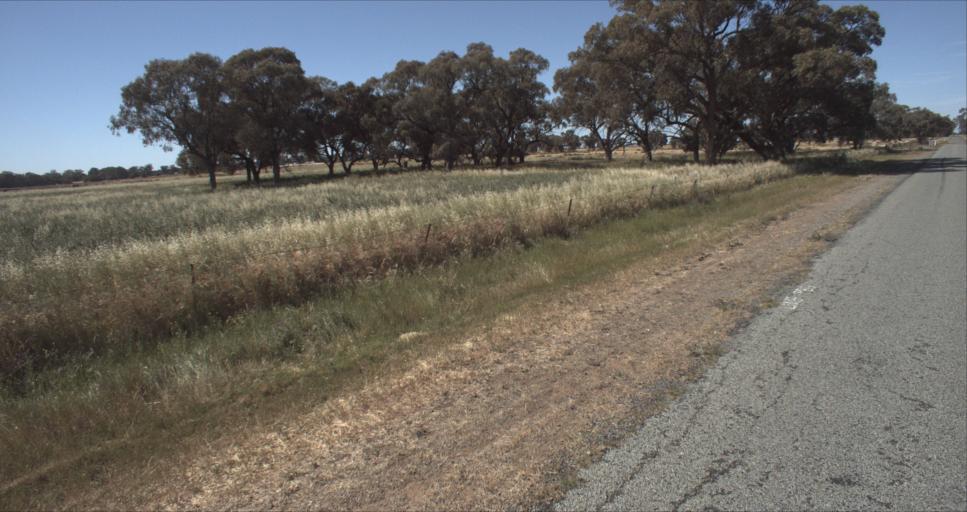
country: AU
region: New South Wales
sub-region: Leeton
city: Leeton
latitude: -34.5385
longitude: 146.3169
